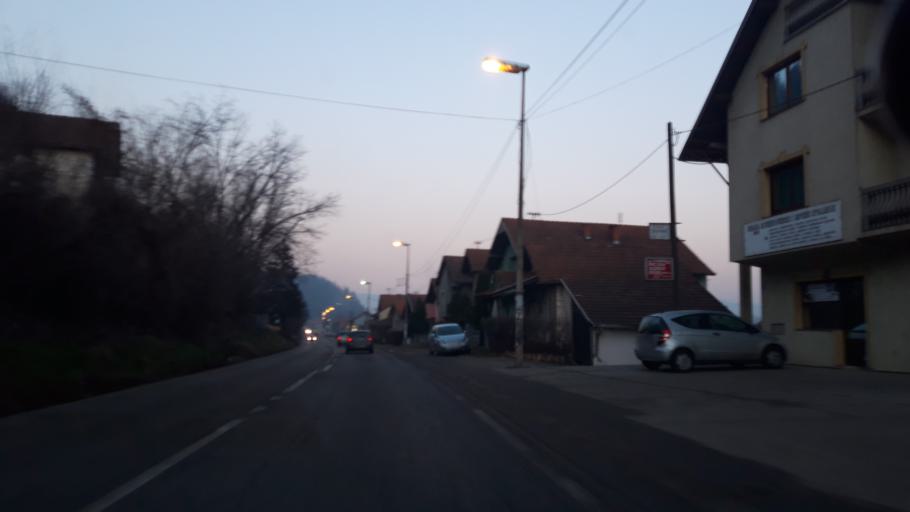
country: BA
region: Republika Srpska
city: Zvornik
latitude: 44.4014
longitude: 19.1139
